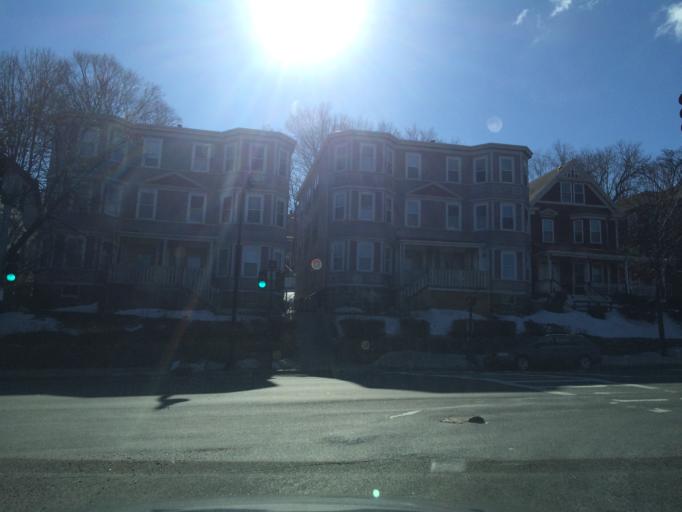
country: US
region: Massachusetts
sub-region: Suffolk County
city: Jamaica Plain
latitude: 42.2980
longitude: -71.1151
